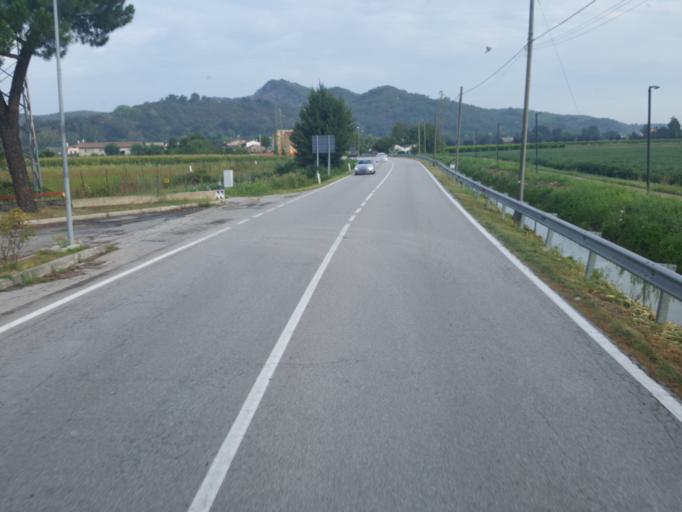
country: IT
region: Veneto
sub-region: Provincia di Padova
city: Battaglia Terme
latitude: 45.2960
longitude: 11.7994
